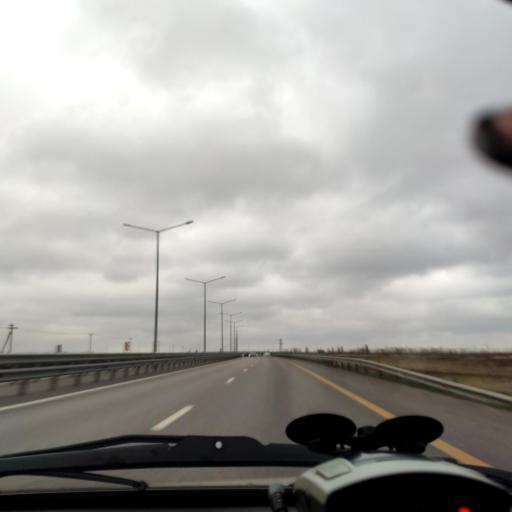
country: RU
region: Voronezj
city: Novaya Usman'
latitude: 51.5925
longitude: 39.3658
